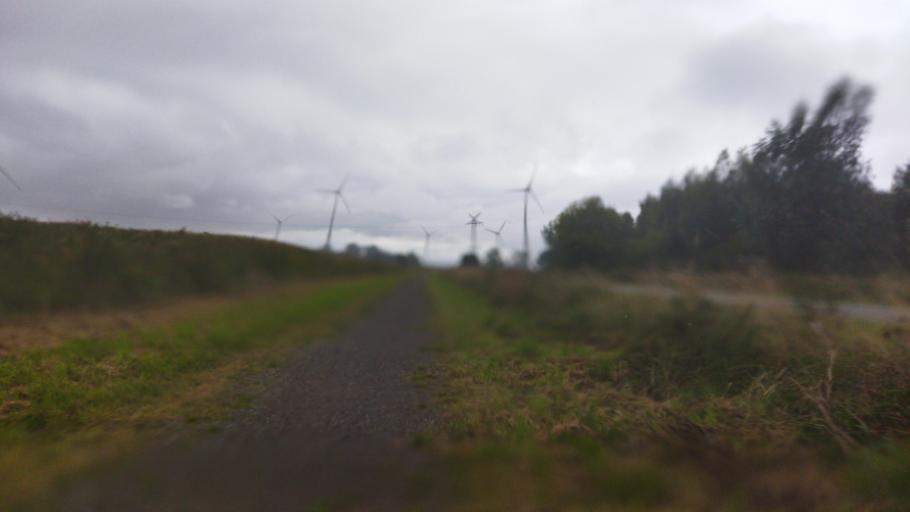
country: DE
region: Lower Saxony
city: Emden
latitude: 53.3473
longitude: 7.1403
